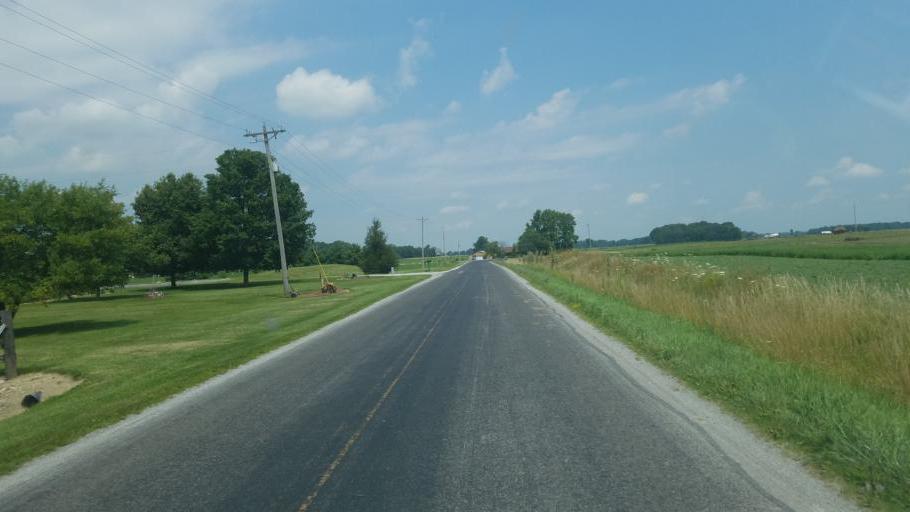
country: US
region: Ohio
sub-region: Hardin County
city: Kenton
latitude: 40.5603
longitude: -83.4417
